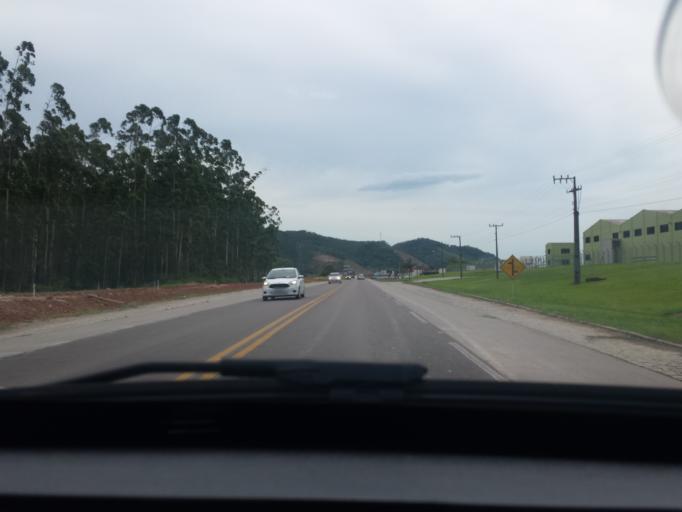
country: BR
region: Santa Catarina
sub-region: Gaspar
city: Gaspar
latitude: -26.9001
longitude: -48.9286
